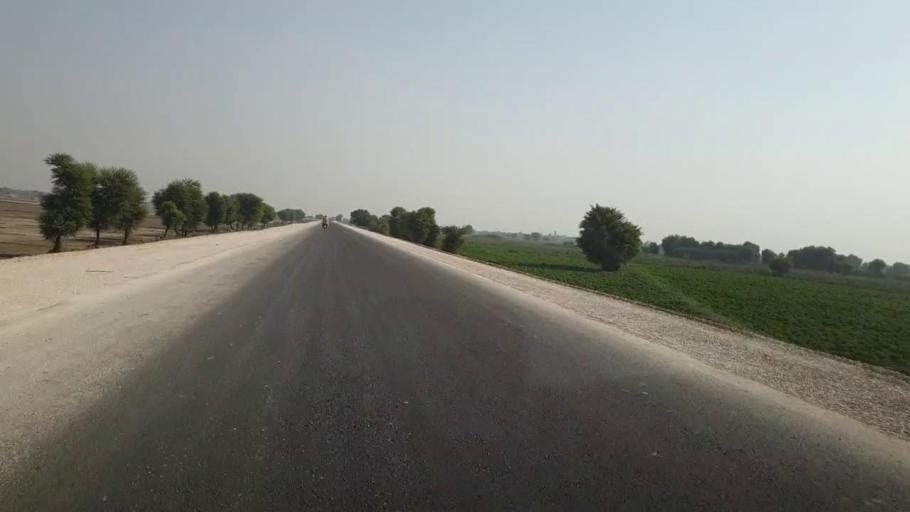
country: PK
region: Sindh
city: Bhan
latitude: 26.5588
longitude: 67.7755
